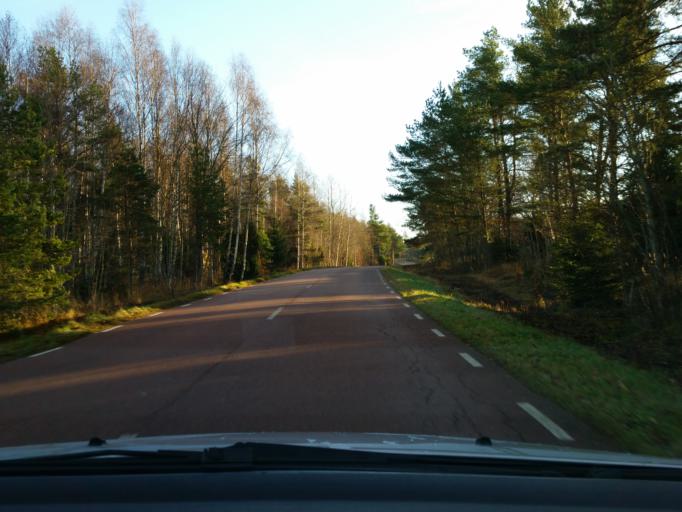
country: AX
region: Alands landsbygd
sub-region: Sund
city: Sund
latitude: 60.2800
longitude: 20.0991
